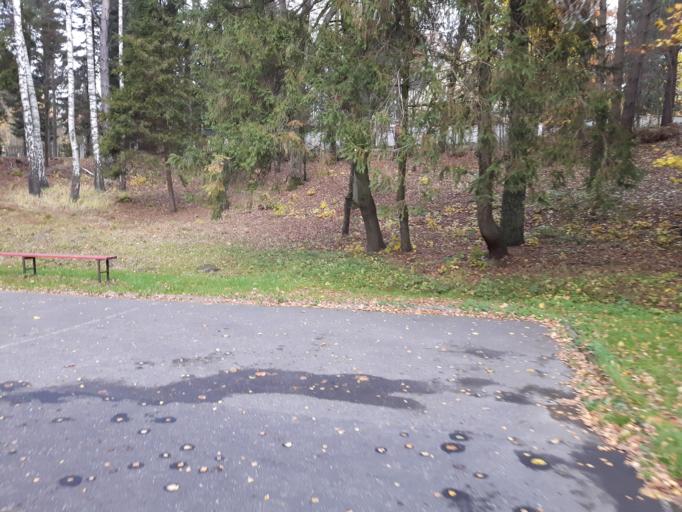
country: PL
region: Warmian-Masurian Voivodeship
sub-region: Powiat olsztynski
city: Barczewo
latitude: 53.8299
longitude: 20.7385
